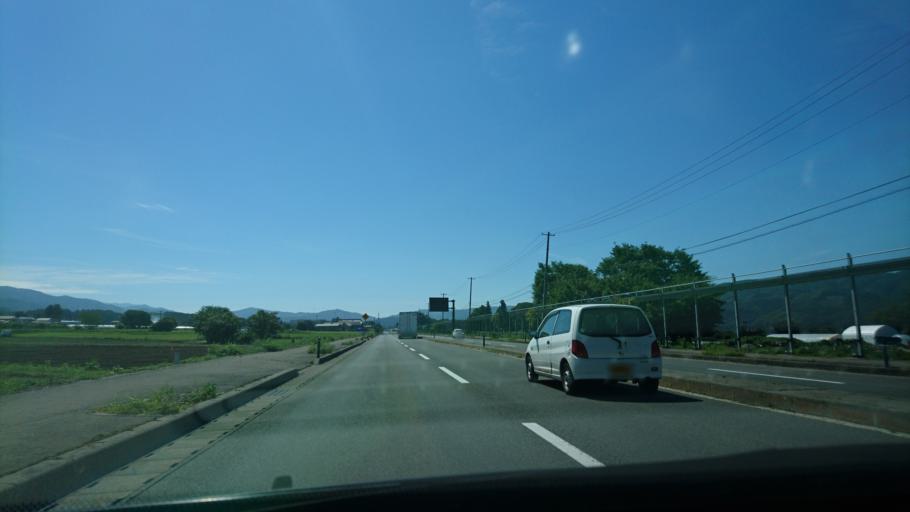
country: JP
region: Iwate
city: Tono
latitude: 39.3235
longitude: 141.5651
